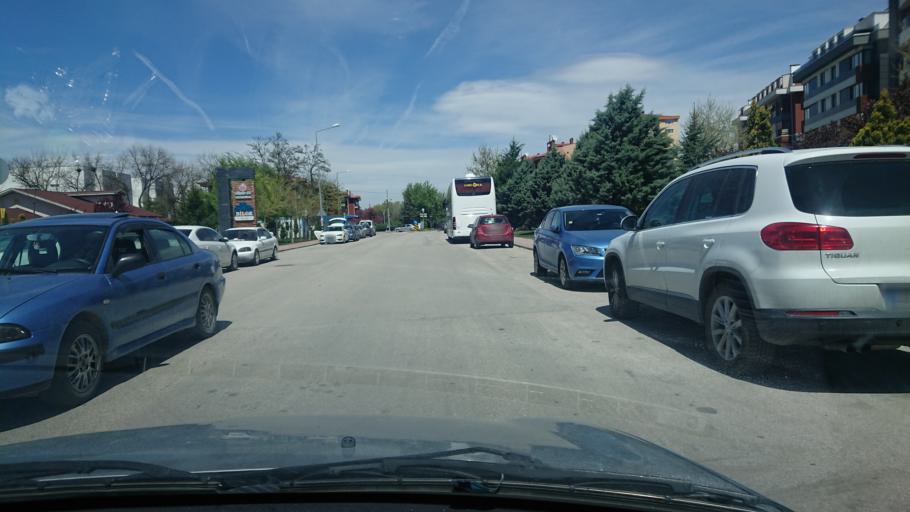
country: TR
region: Eskisehir
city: Eskisehir
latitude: 39.7660
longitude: 30.4971
